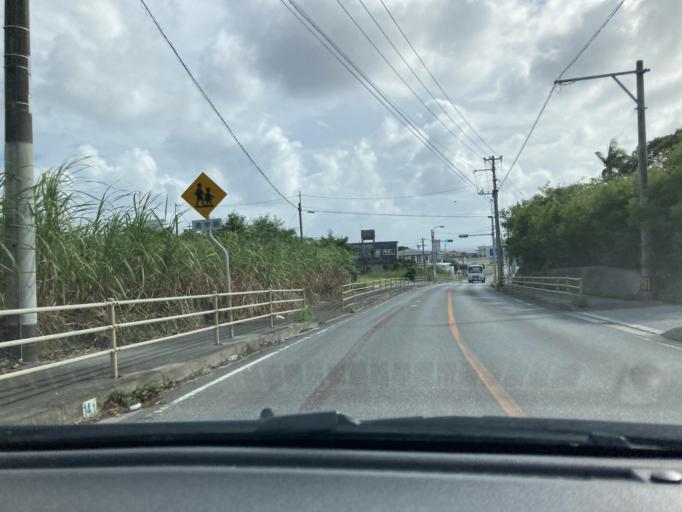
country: JP
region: Okinawa
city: Itoman
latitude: 26.0977
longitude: 127.6995
